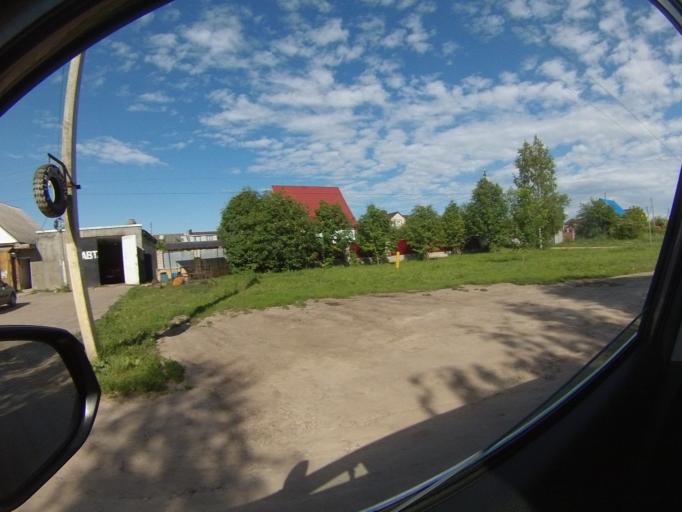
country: RU
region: Orjol
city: Mtsensk
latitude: 53.2975
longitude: 36.6031
